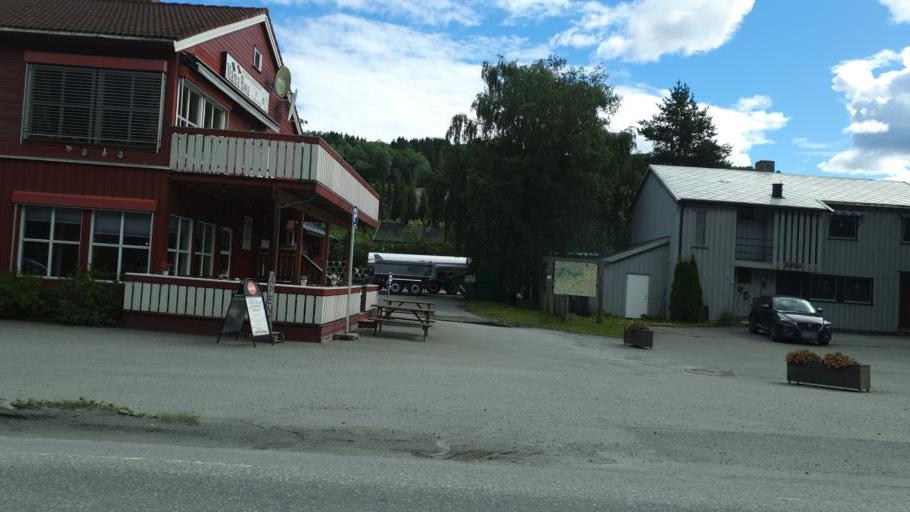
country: NO
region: Sor-Trondelag
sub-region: Midtre Gauldal
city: Storen
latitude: 62.9488
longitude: 10.1895
